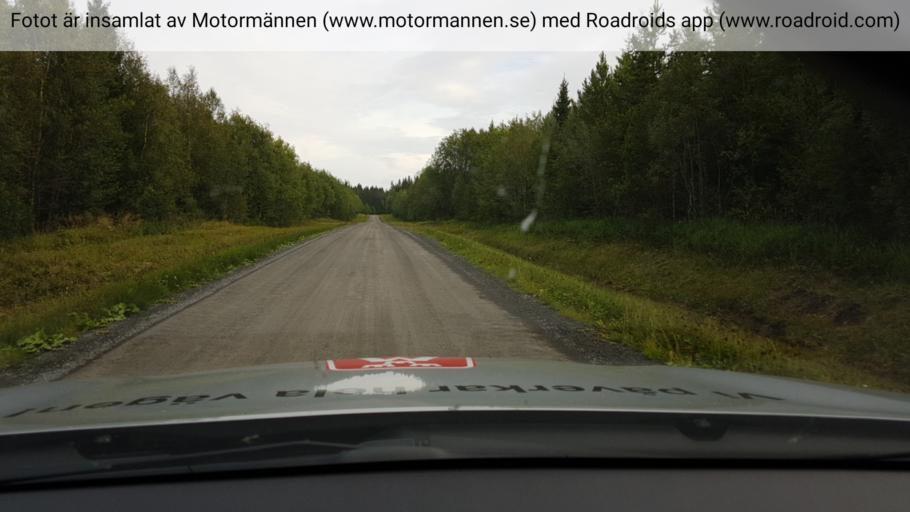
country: SE
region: Jaemtland
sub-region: OEstersunds Kommun
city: Lit
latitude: 63.6497
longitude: 14.9427
